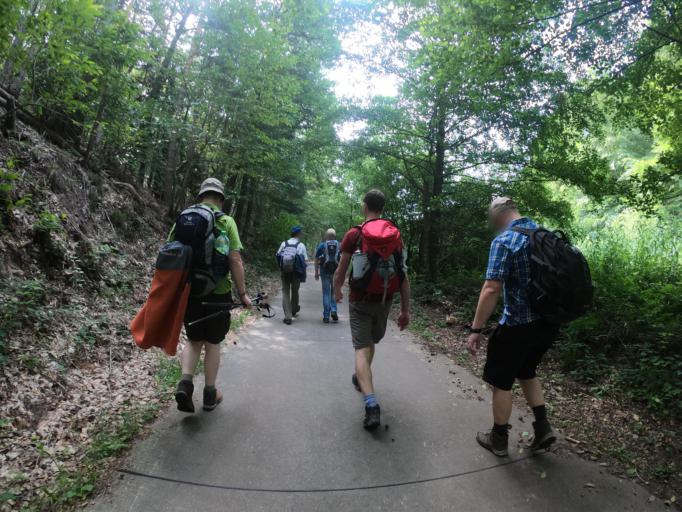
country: DE
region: Rheinland-Pfalz
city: Gleiszellen-Gleishorbach
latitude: 49.1195
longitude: 7.9813
